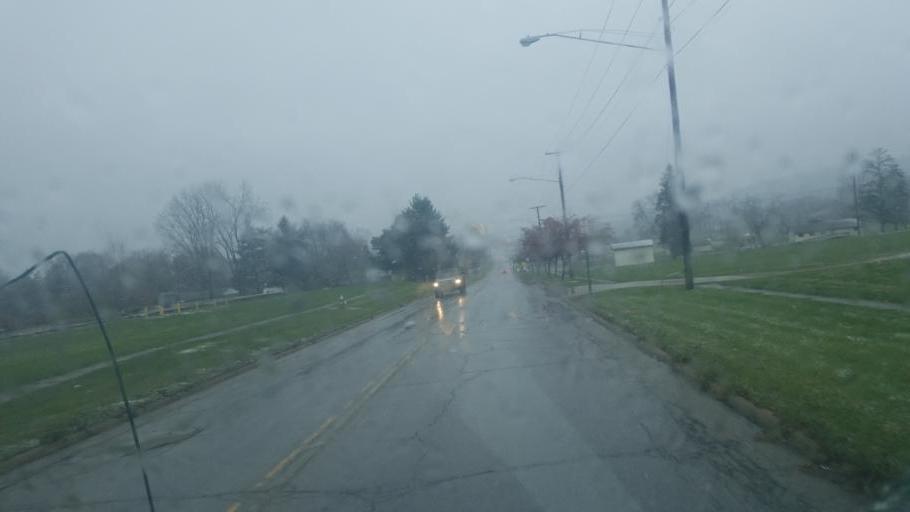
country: US
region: Ohio
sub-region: Richland County
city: Lexington
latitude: 40.6827
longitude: -82.5837
